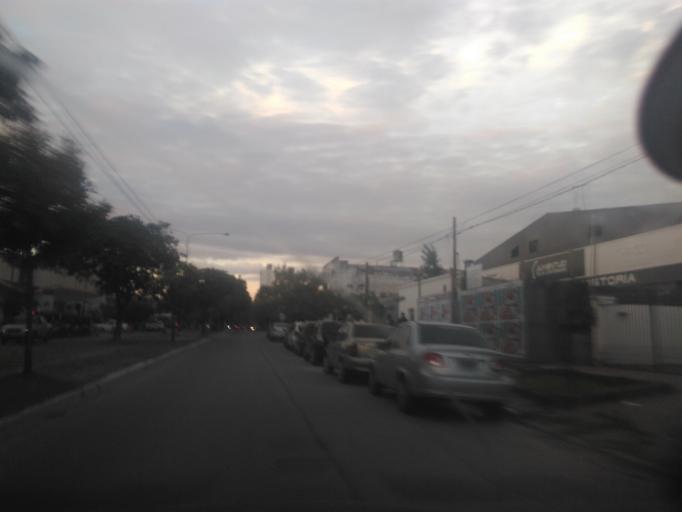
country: AR
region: Chaco
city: Resistencia
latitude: -27.4637
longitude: -58.9917
